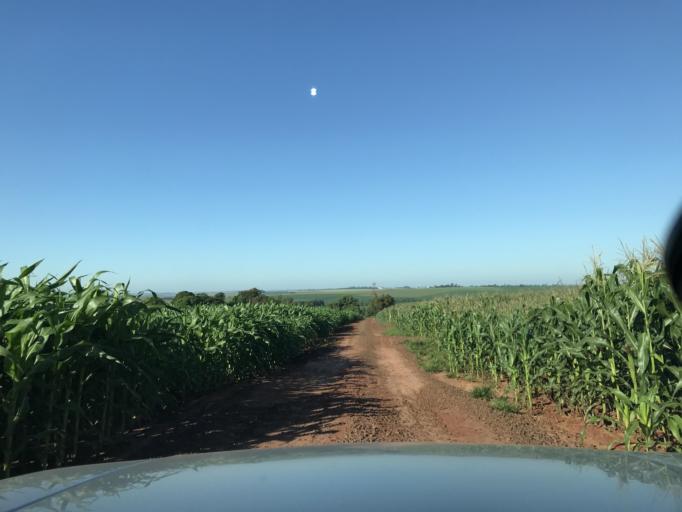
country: BR
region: Parana
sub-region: Palotina
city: Palotina
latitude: -24.2332
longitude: -53.7639
